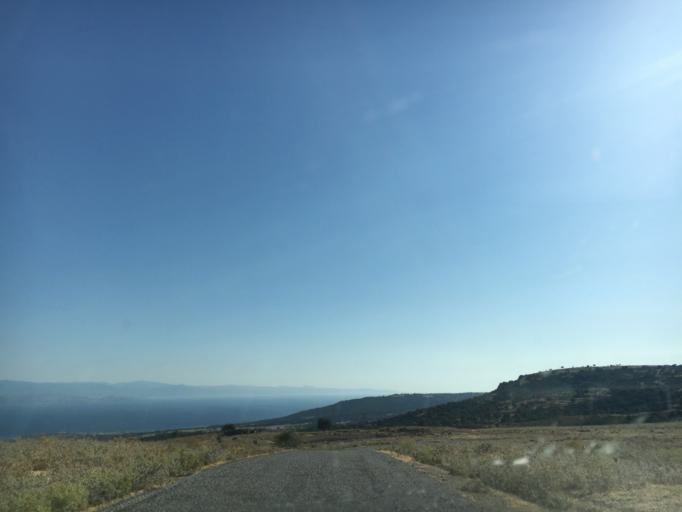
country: TR
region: Canakkale
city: Behram
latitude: 39.5007
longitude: 26.2584
